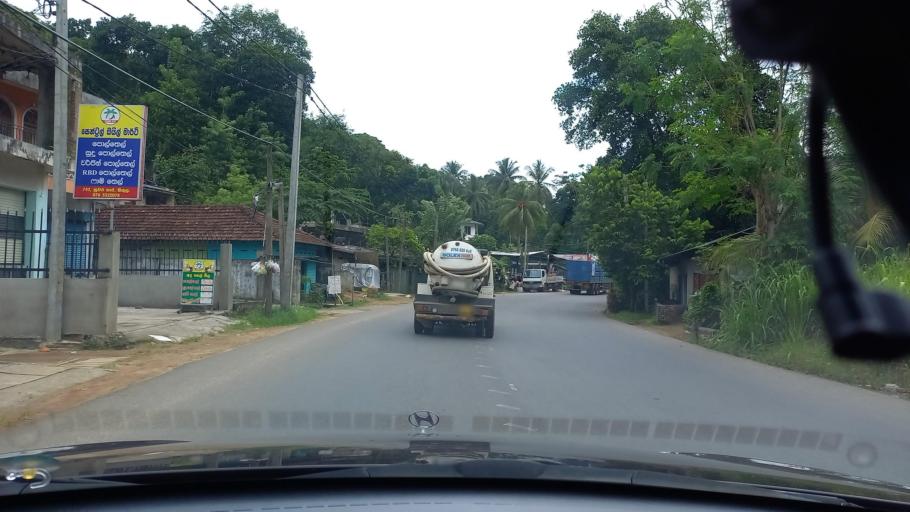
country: LK
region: Central
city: Kadugannawa
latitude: 7.2475
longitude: 80.4729
